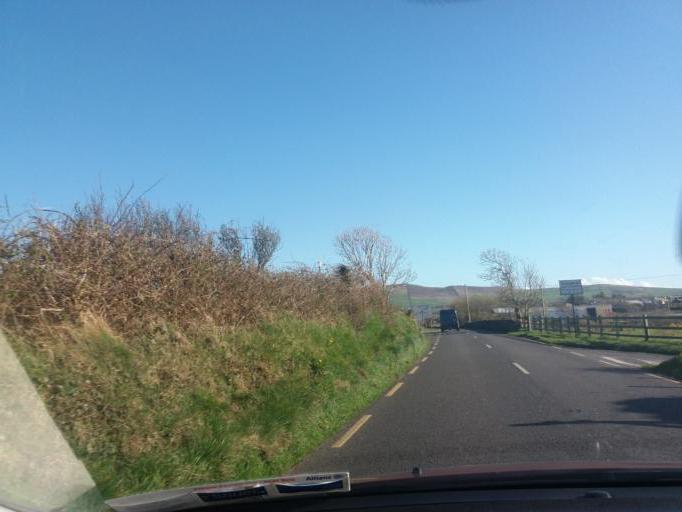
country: IE
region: Munster
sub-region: Ciarrai
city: Dingle
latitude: 52.1458
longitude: -10.2890
